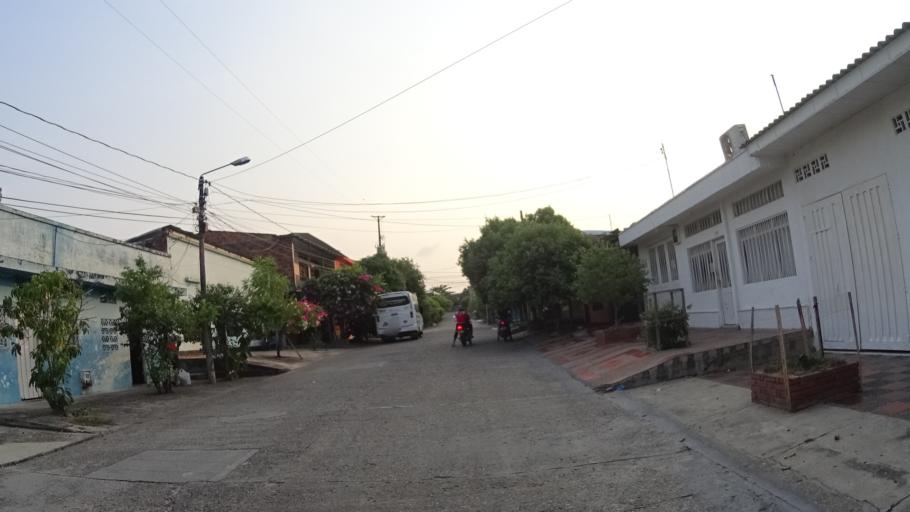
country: CO
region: Caldas
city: La Dorada
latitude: 5.4508
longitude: -74.6700
